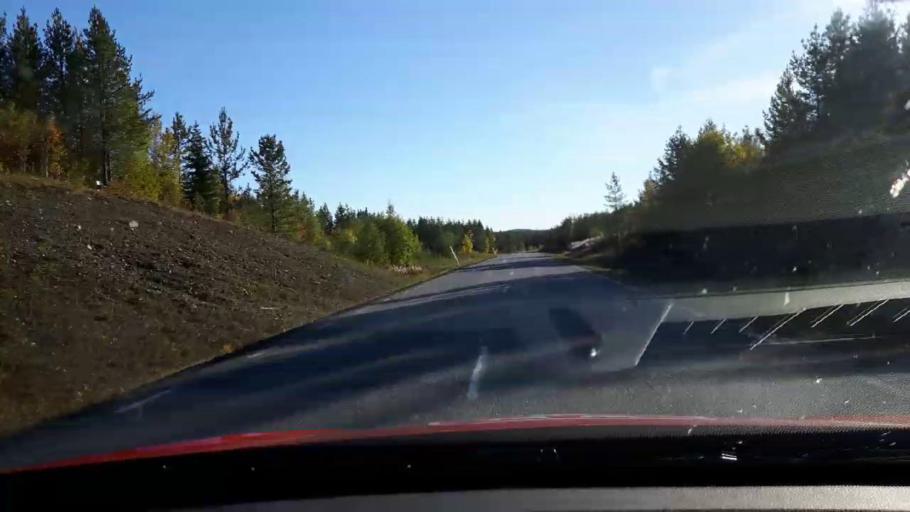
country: SE
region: Jaemtland
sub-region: OEstersunds Kommun
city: Lit
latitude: 63.8451
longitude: 14.9173
